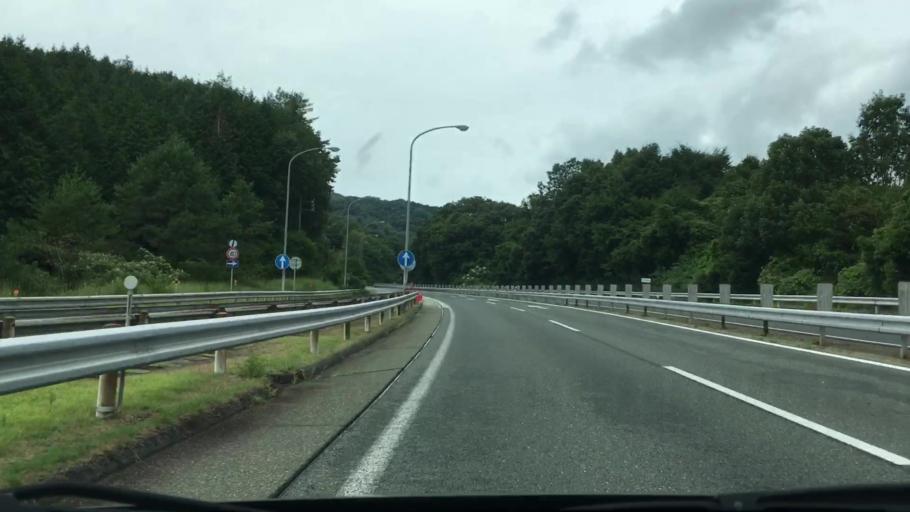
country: JP
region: Okayama
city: Niimi
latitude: 34.8939
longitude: 133.2530
